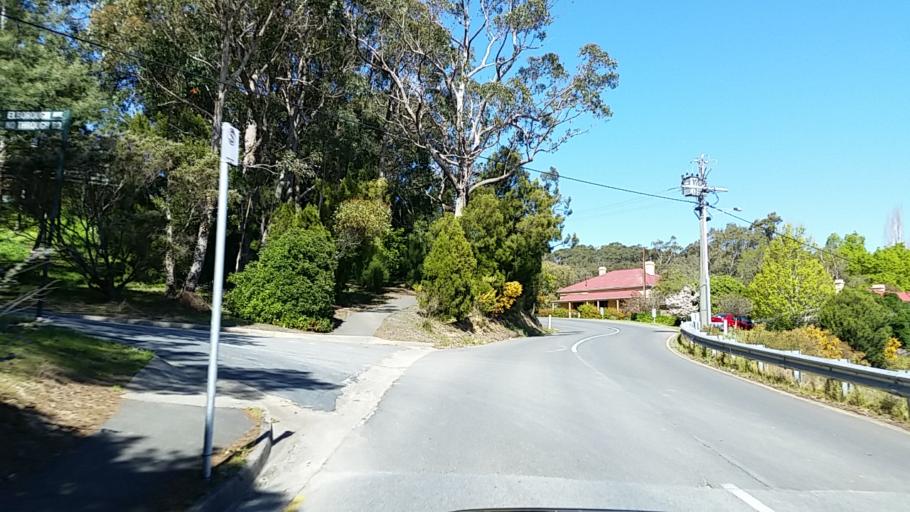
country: AU
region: South Australia
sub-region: Adelaide Hills
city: Bridgewater
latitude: -34.9567
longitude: 138.7457
